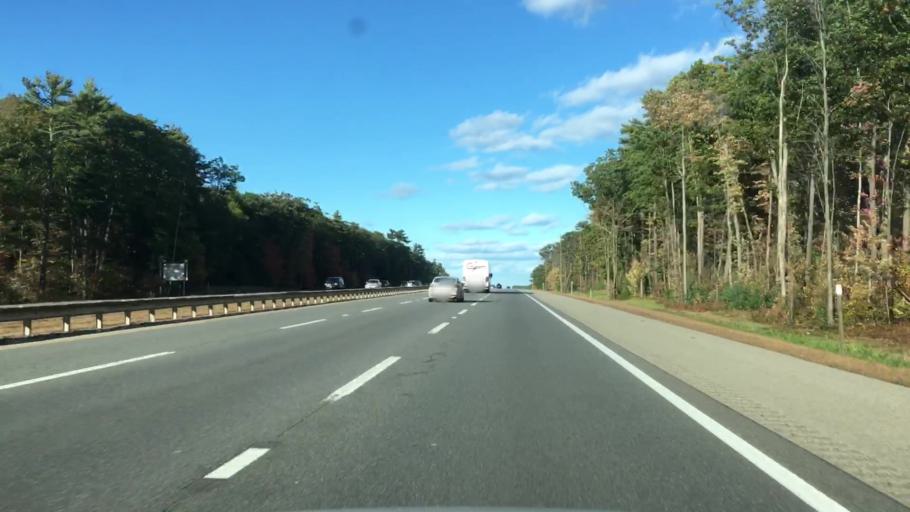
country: US
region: Maine
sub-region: York County
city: Wells Beach Station
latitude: 43.3625
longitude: -70.5861
